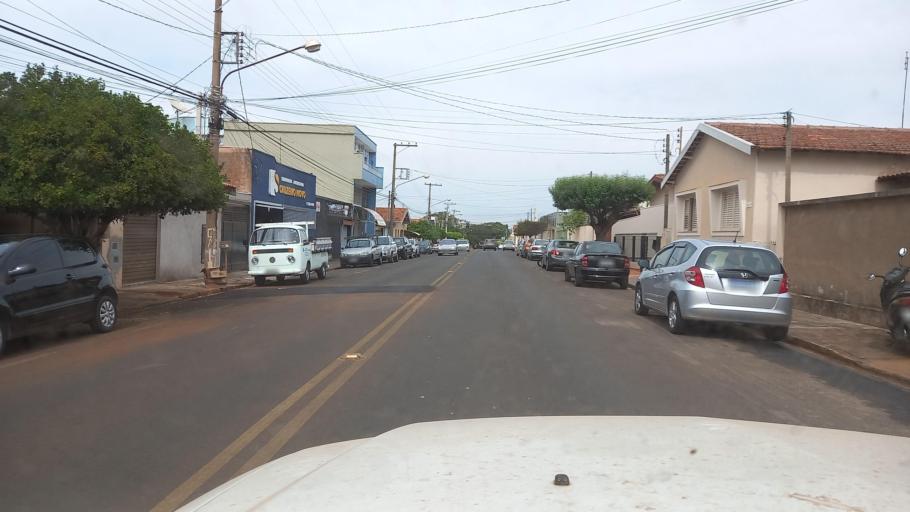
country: BR
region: Sao Paulo
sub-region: Moji-Guacu
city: Mogi-Gaucu
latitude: -22.3606
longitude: -46.9423
